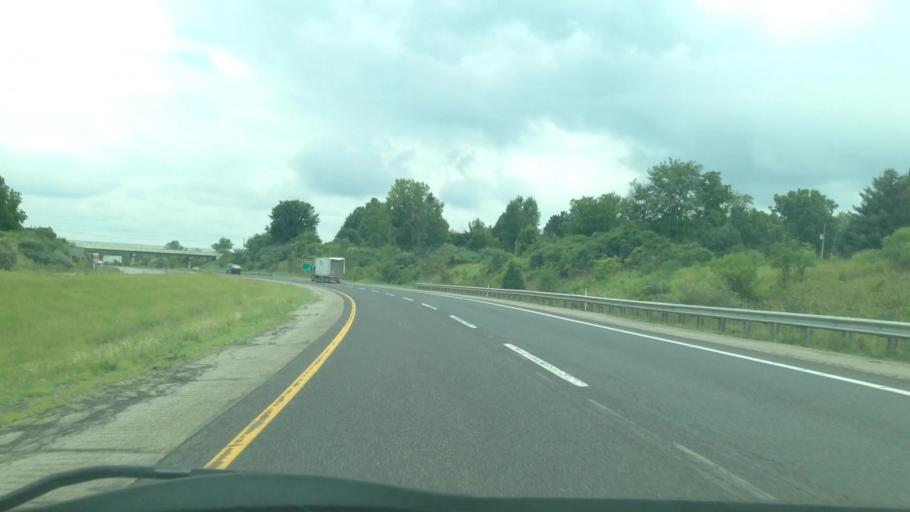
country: US
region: Indiana
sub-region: Steuben County
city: Fremont
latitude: 41.7349
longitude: -84.9765
